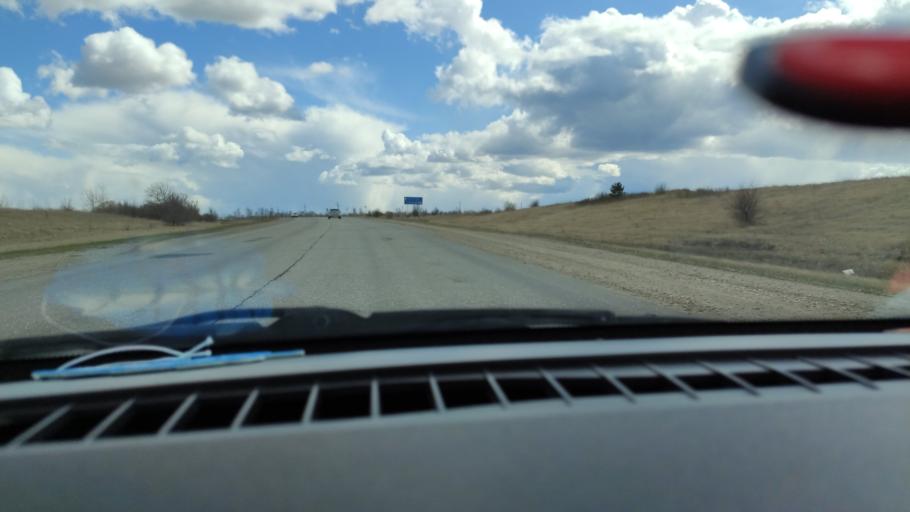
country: RU
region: Samara
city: Varlamovo
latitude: 53.1245
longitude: 48.2946
